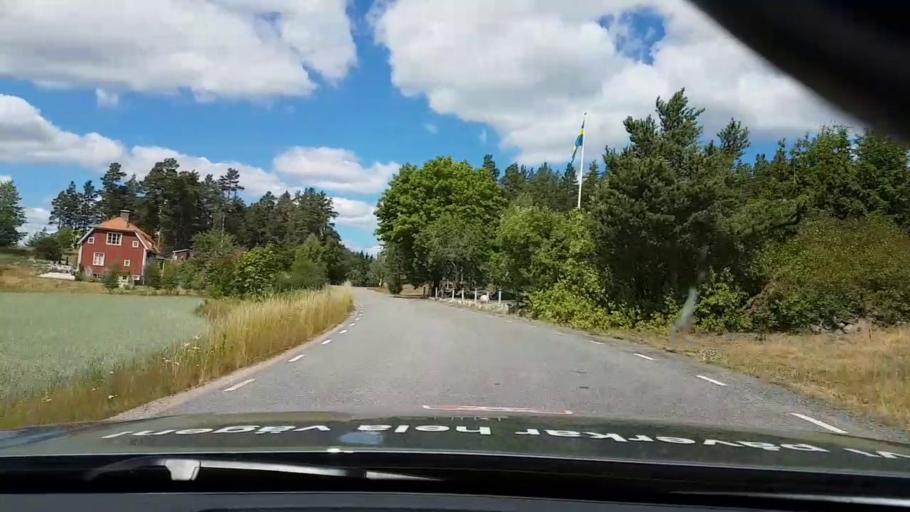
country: SE
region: Kalmar
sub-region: Vasterviks Kommun
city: Forserum
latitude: 58.0182
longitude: 16.5761
